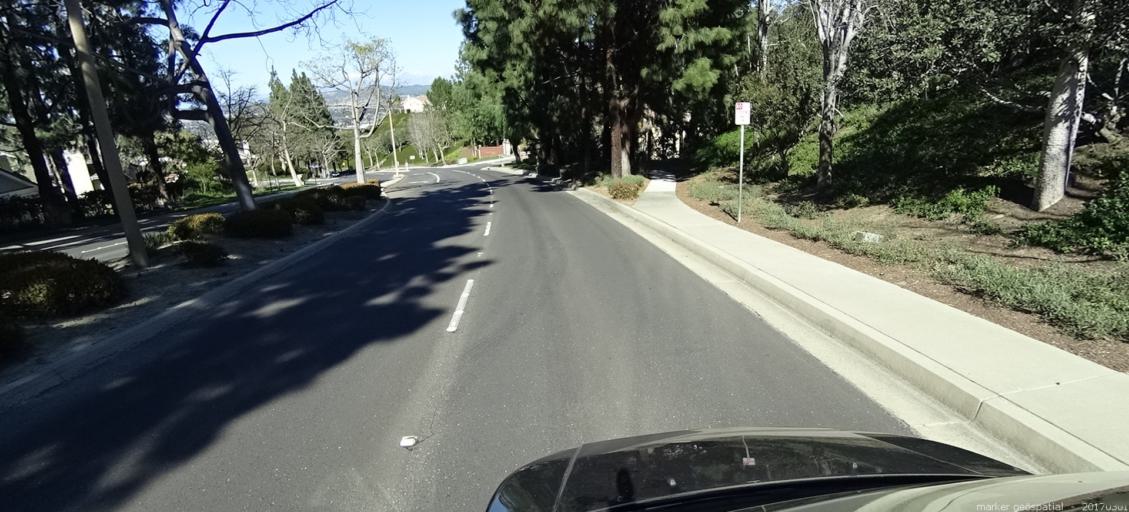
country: US
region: California
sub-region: Orange County
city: Villa Park
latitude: 33.8384
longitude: -117.8098
